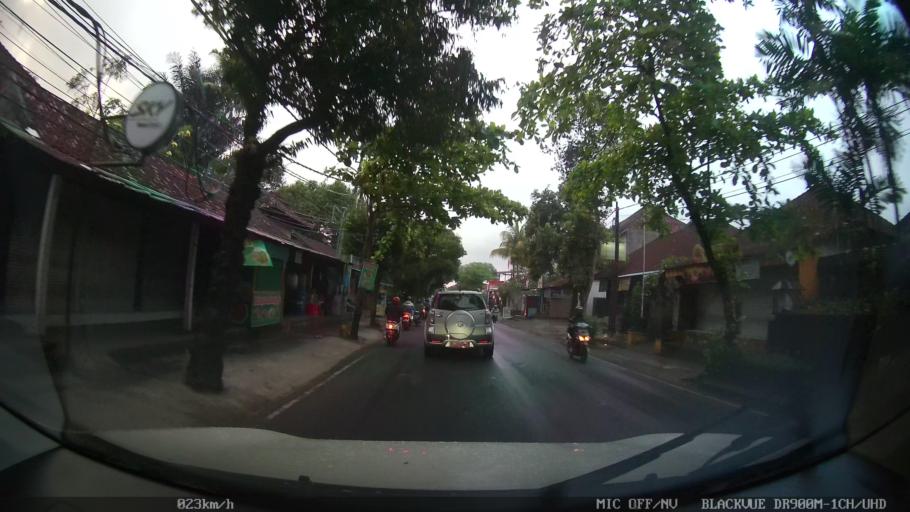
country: ID
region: Bali
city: Banjar Bucu
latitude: -8.5878
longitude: 115.2157
